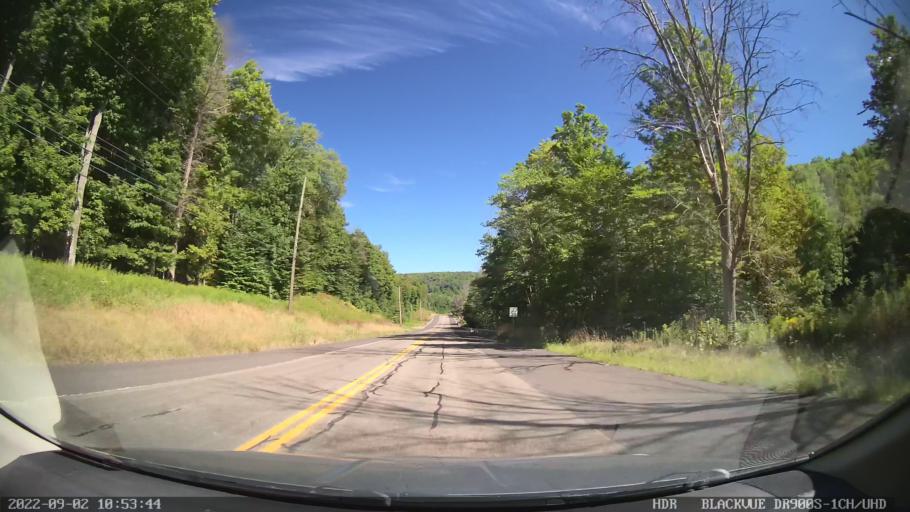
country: US
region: Pennsylvania
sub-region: Tioga County
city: Blossburg
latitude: 41.6499
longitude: -77.0956
